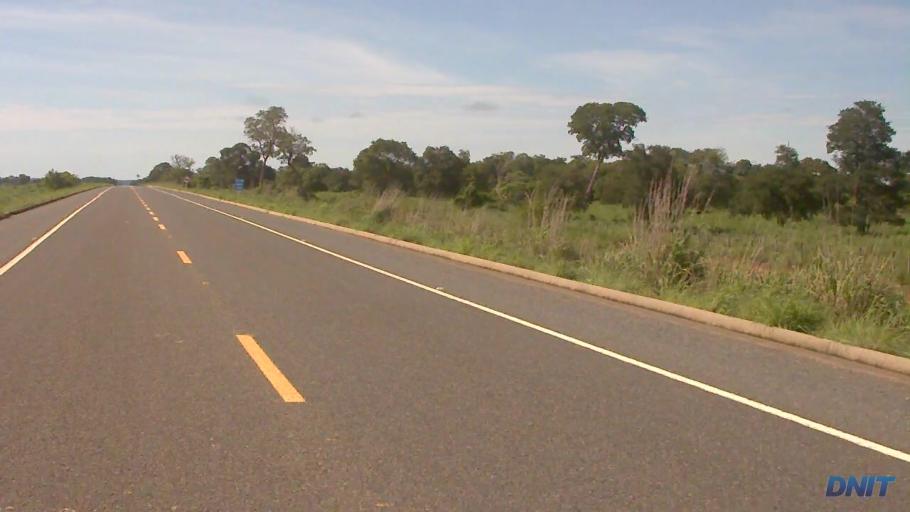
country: BR
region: Goias
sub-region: Sao Miguel Do Araguaia
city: Sao Miguel do Araguaia
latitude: -13.4326
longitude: -50.1259
